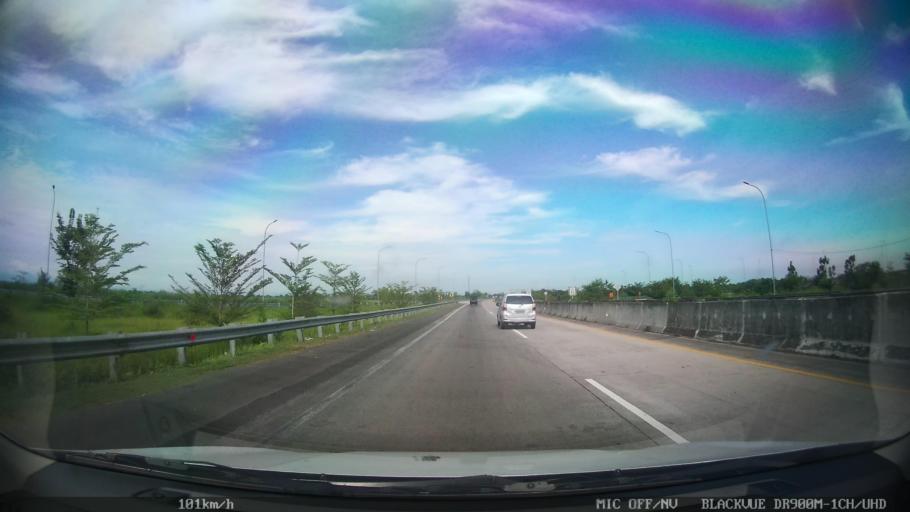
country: ID
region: North Sumatra
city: Sunggal
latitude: 3.6373
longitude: 98.5822
